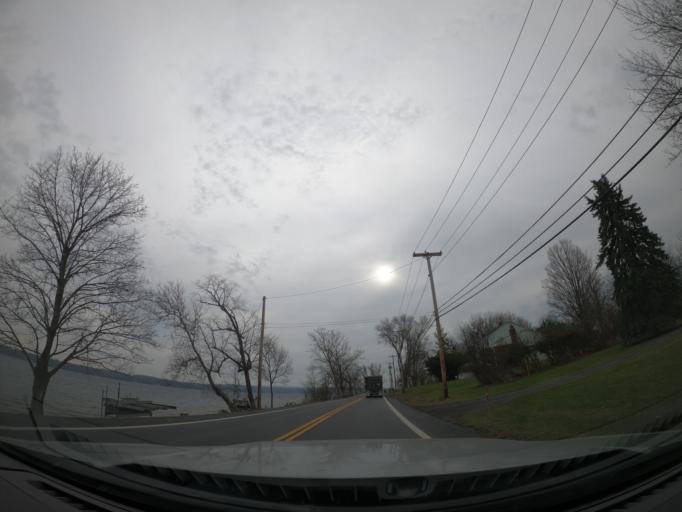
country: US
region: New York
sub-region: Cayuga County
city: Melrose Park
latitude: 42.8703
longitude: -76.5352
